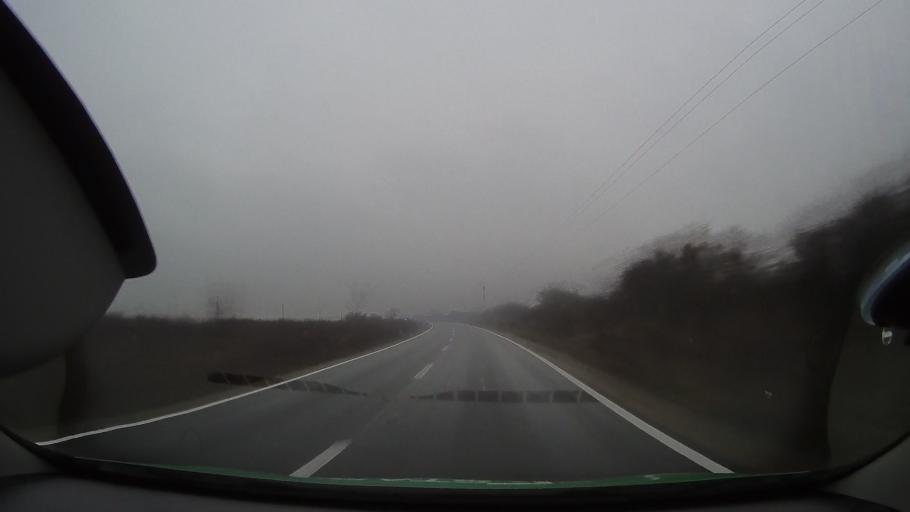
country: RO
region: Bihor
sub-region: Comuna Tinca
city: Tinca
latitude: 46.7269
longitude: 21.9442
